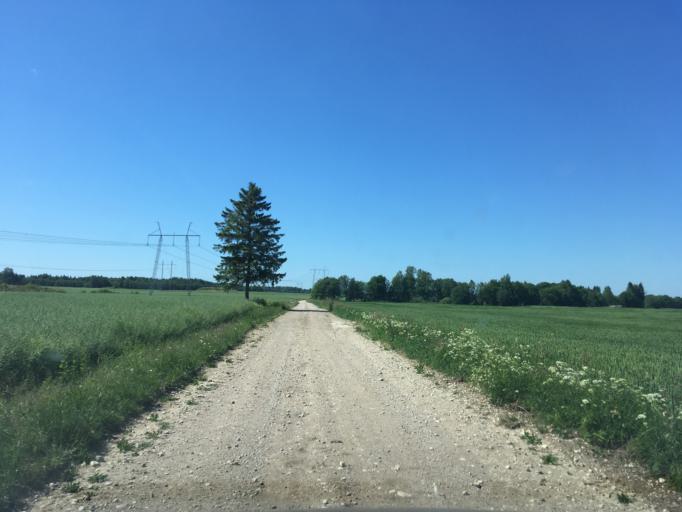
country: EE
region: Harju
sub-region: Anija vald
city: Kehra
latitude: 59.2548
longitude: 25.3068
